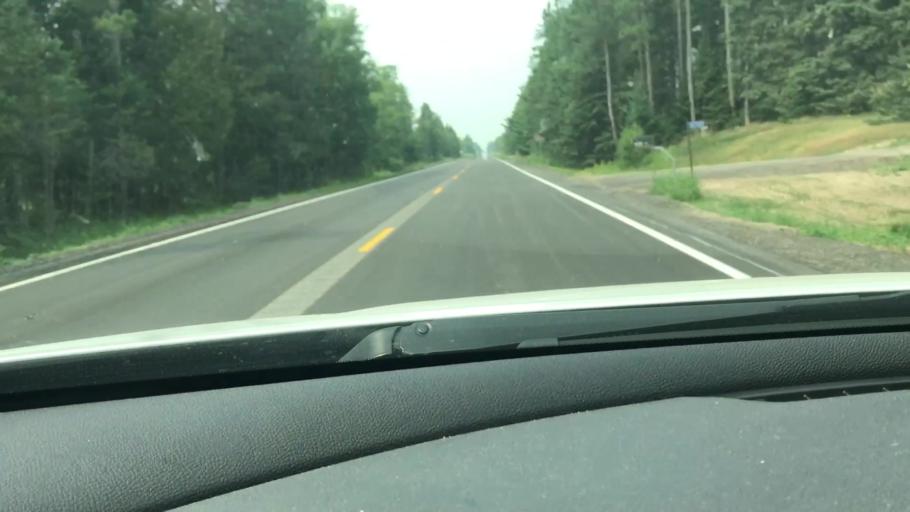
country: US
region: Minnesota
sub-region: Itasca County
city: Cohasset
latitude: 47.3498
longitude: -93.8364
